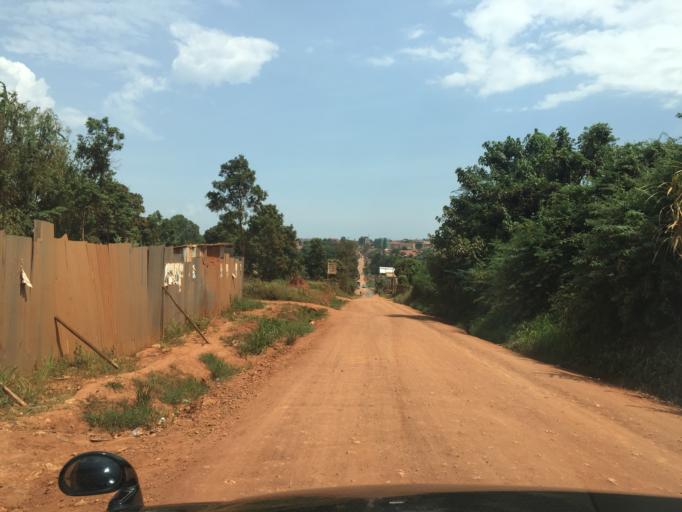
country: UG
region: Central Region
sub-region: Wakiso District
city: Kireka
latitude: 0.3979
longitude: 32.6225
